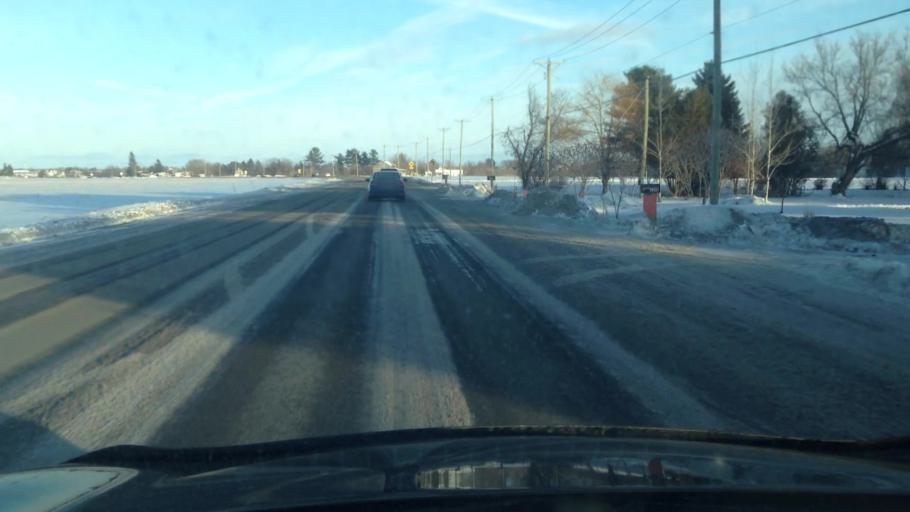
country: CA
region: Quebec
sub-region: Lanaudiere
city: Saint-Lin-Laurentides
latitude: 45.8446
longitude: -73.7975
